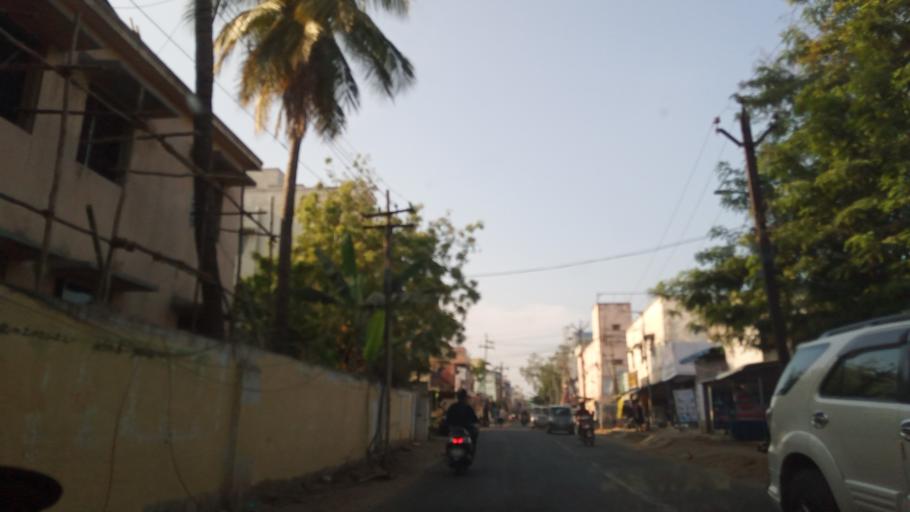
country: IN
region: Tamil Nadu
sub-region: Kancheepuram
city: Manappakkam
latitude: 13.0256
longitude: 80.1831
